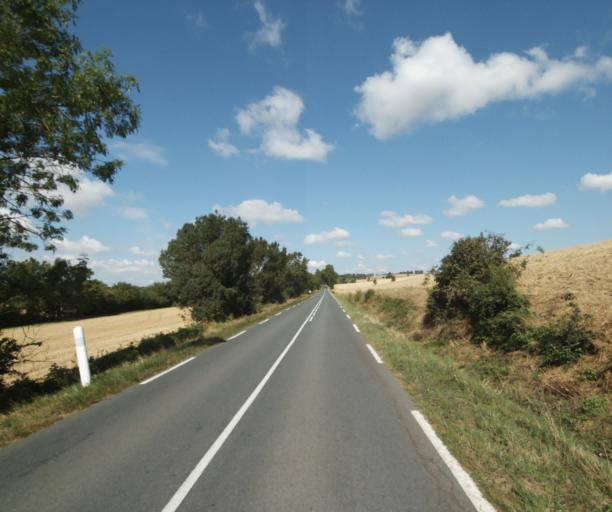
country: FR
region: Midi-Pyrenees
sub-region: Departement de la Haute-Garonne
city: Avignonet-Lauragais
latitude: 43.4448
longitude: 1.8065
